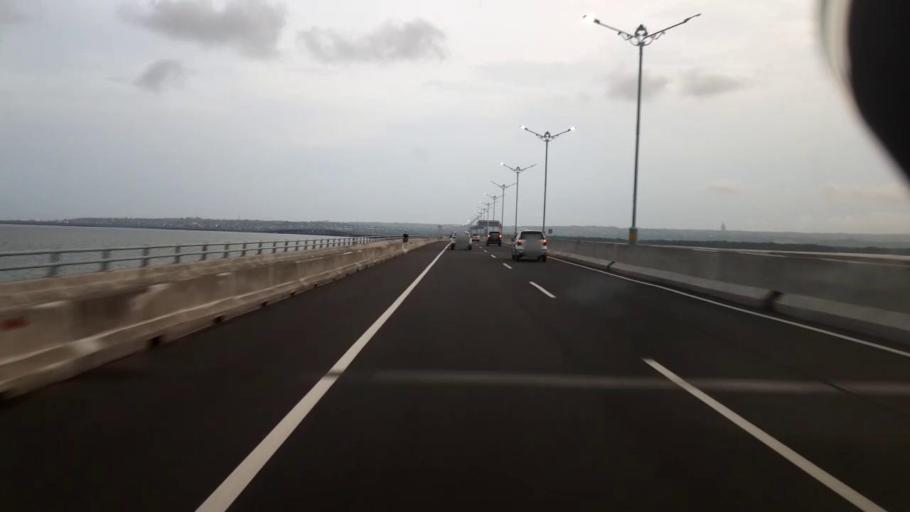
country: ID
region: Bali
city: Kelanabian
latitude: -8.7520
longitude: 115.1955
